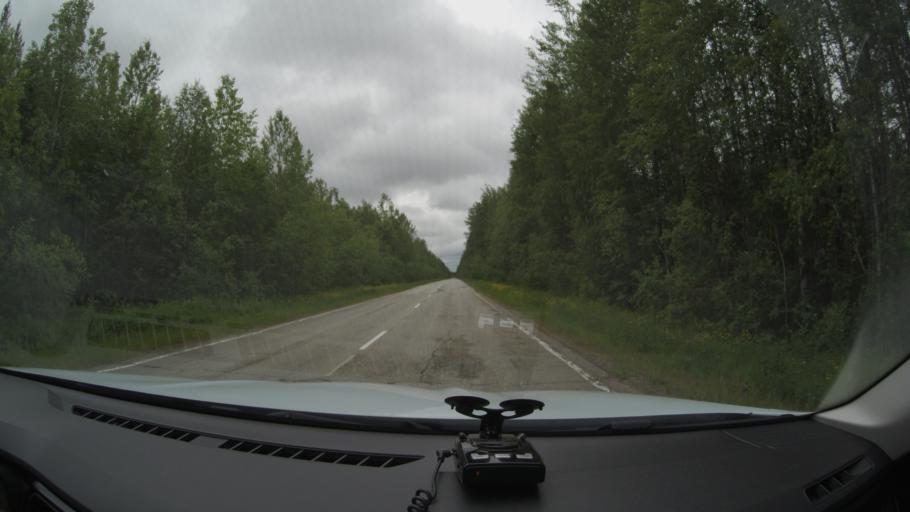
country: RU
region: Komi Republic
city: Nizhniy Odes
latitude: 63.6251
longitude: 54.6214
